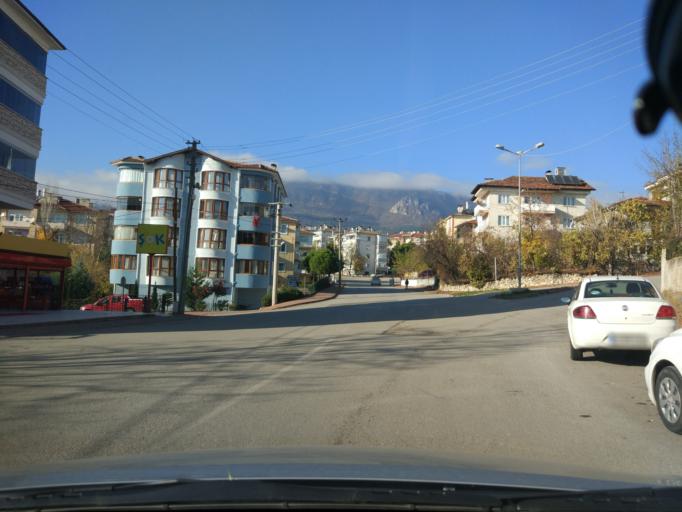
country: TR
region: Karabuk
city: Safranbolu
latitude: 41.2519
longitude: 32.6720
